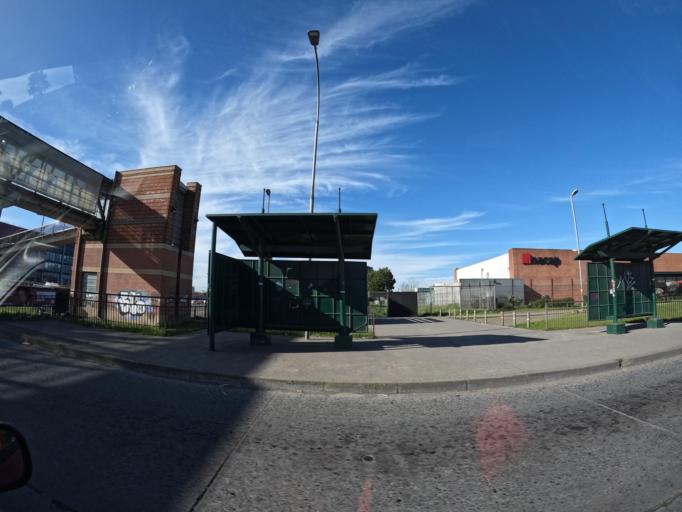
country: CL
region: Biobio
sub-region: Provincia de Concepcion
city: Concepcion
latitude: -36.7814
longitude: -73.0764
